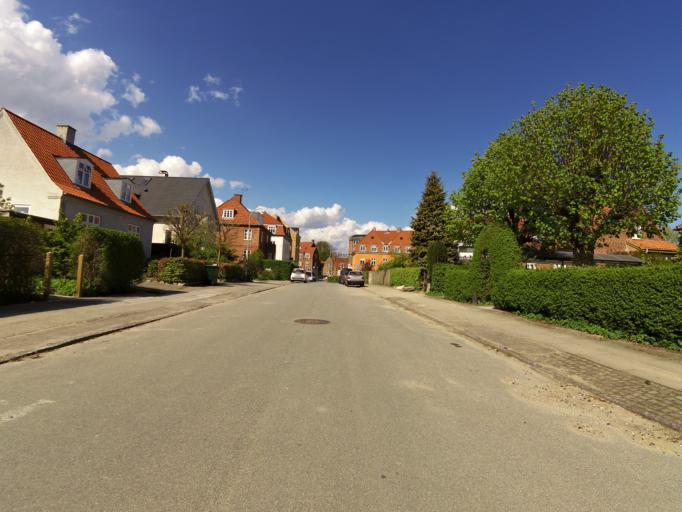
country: DK
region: Capital Region
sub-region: Gladsaxe Municipality
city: Buddinge
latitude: 55.7306
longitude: 12.5188
